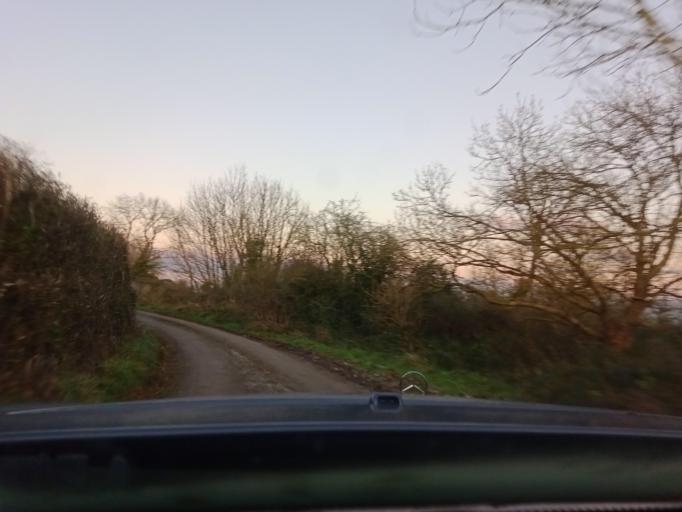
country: IE
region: Leinster
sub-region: Kilkenny
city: Graiguenamanagh
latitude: 52.5764
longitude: -6.9594
